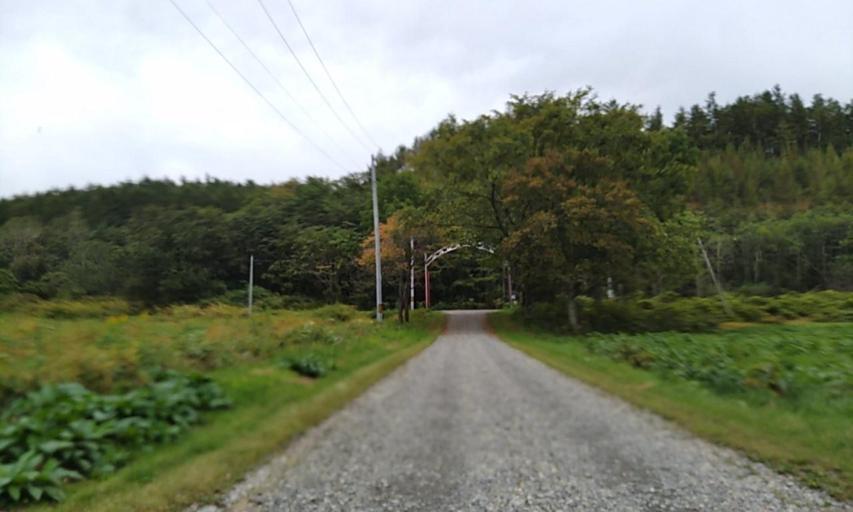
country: JP
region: Hokkaido
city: Obihiro
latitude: 42.6685
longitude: 143.0341
